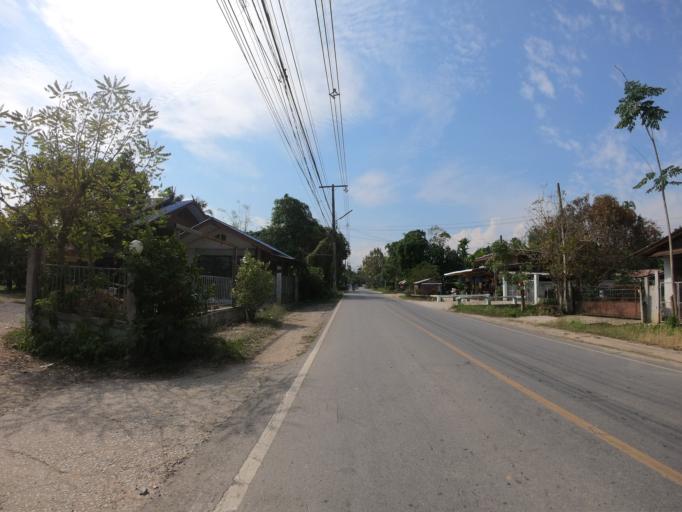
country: TH
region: Chiang Mai
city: San Sai
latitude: 18.8631
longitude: 99.0618
